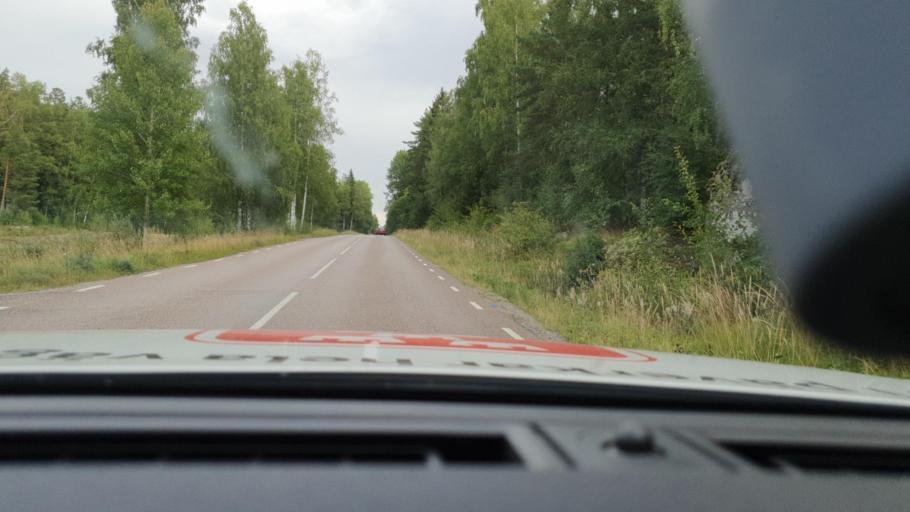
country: SE
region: Uppsala
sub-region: Heby Kommun
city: Tarnsjo
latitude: 60.0853
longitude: 17.0656
